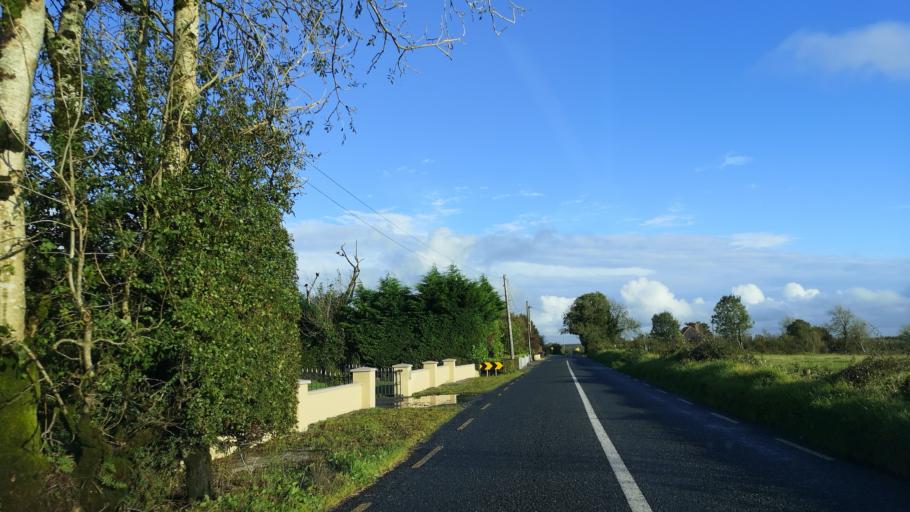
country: IE
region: Connaught
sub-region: Roscommon
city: Castlerea
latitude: 53.8080
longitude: -8.5139
